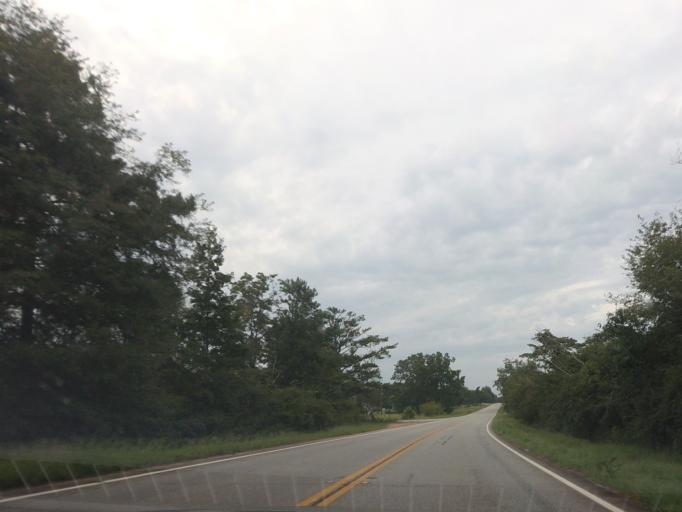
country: US
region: Georgia
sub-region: Twiggs County
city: Jeffersonville
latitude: 32.7243
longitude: -83.4167
